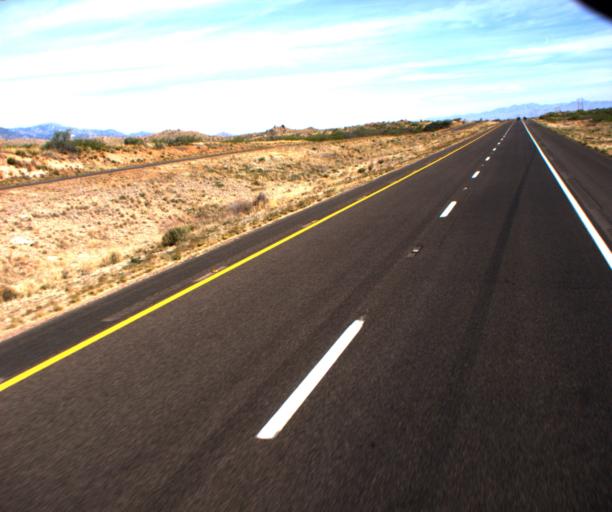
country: US
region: Arizona
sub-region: Graham County
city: Swift Trail Junction
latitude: 32.5119
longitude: -109.6738
